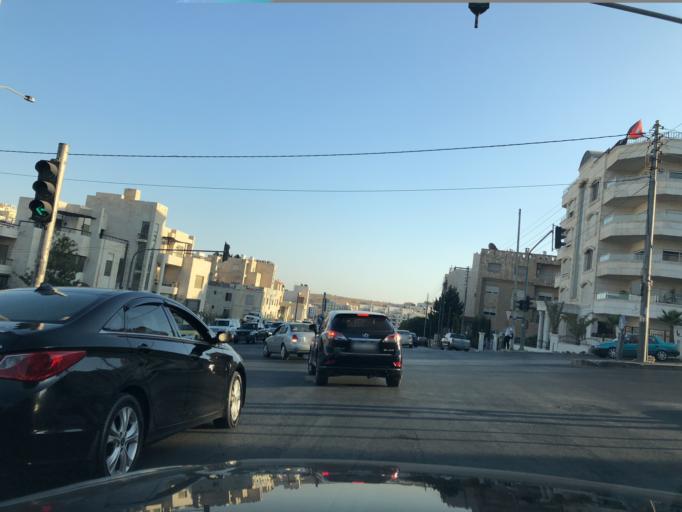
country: JO
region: Amman
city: Wadi as Sir
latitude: 31.9430
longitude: 35.8699
